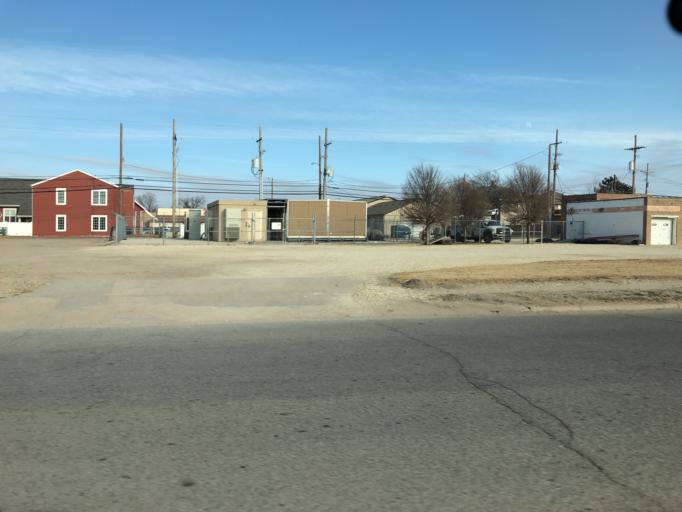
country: US
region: Kansas
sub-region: Reno County
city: Hutchinson
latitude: 38.0573
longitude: -97.9369
